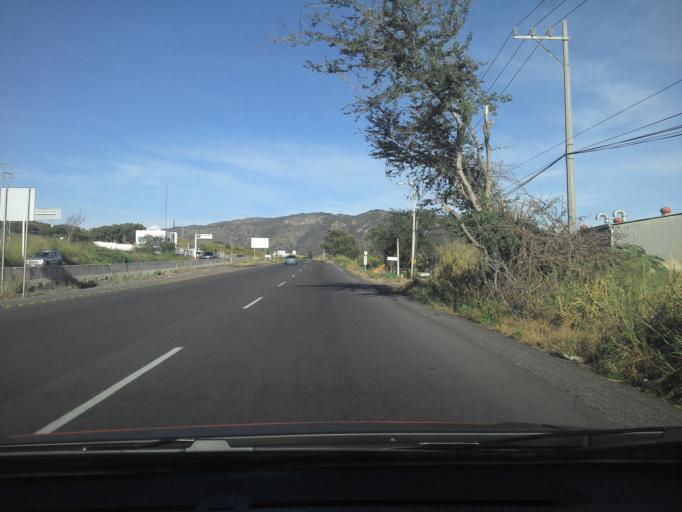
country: MX
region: Jalisco
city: La Venta del Astillero
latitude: 20.7328
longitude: -103.6029
